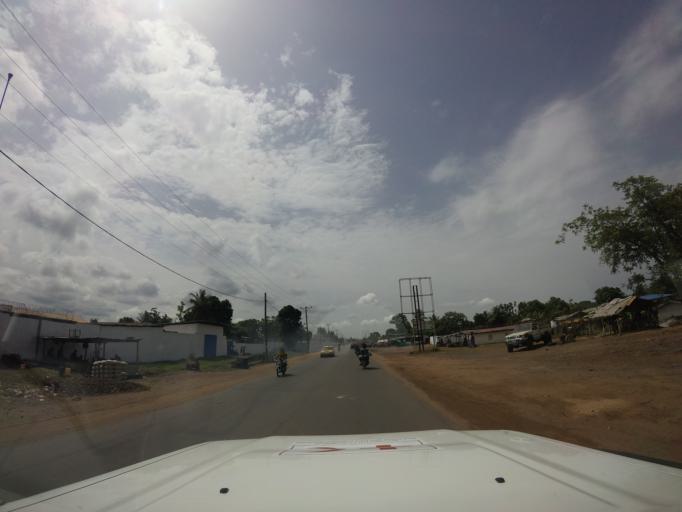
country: LR
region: Montserrado
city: Monrovia
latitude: 6.3926
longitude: -10.7828
